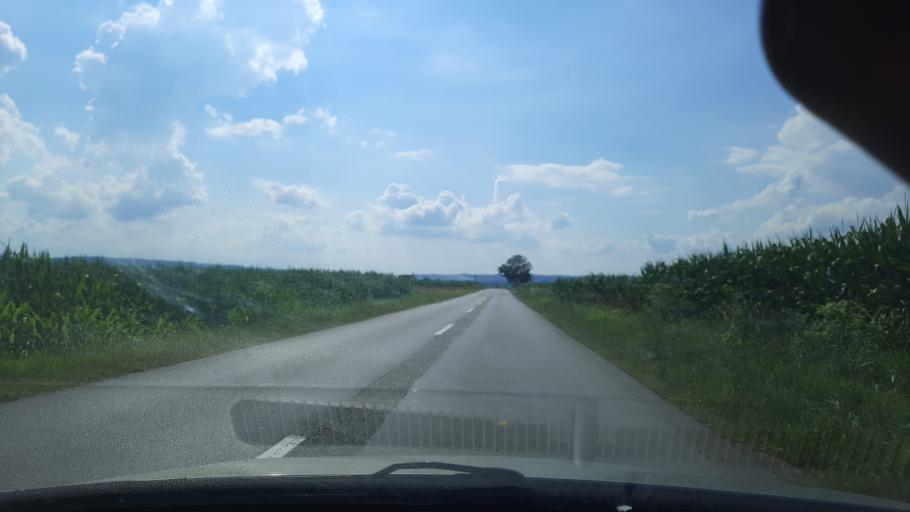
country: RS
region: Central Serbia
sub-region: Branicevski Okrug
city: Malo Crnice
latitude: 44.5843
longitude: 21.2969
